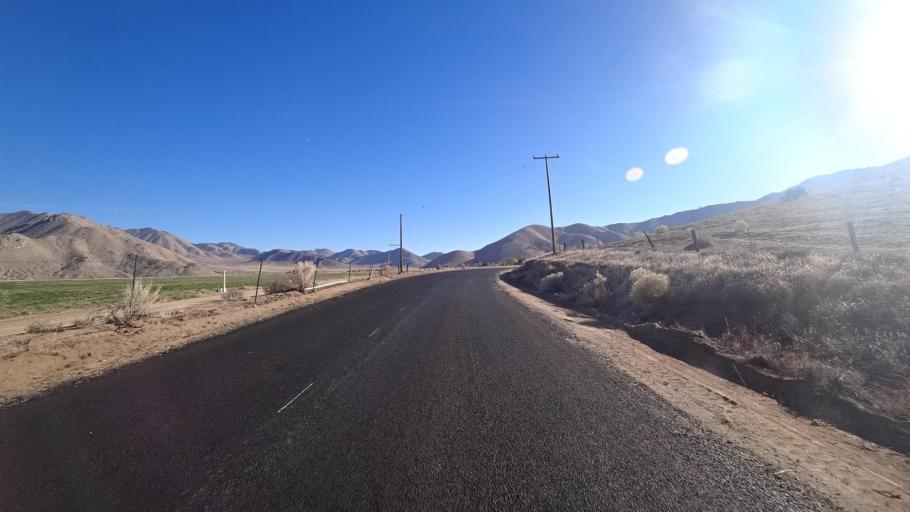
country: US
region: California
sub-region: Kern County
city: Weldon
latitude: 35.6326
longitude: -118.2634
